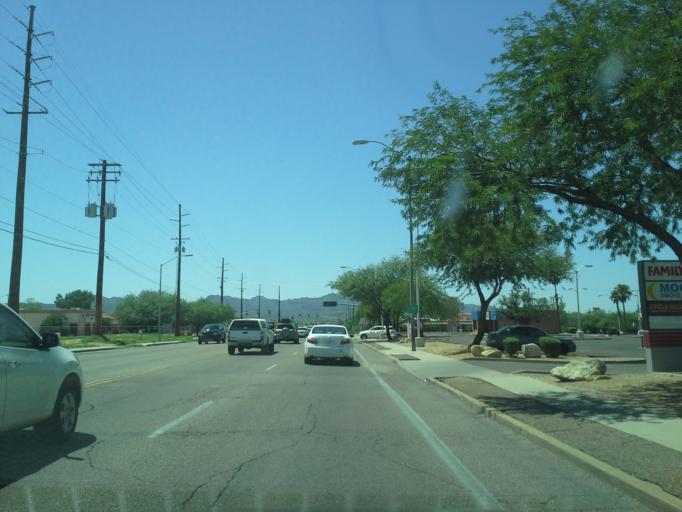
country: US
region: Arizona
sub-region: Pima County
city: South Tucson
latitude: 32.2504
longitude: -110.9724
